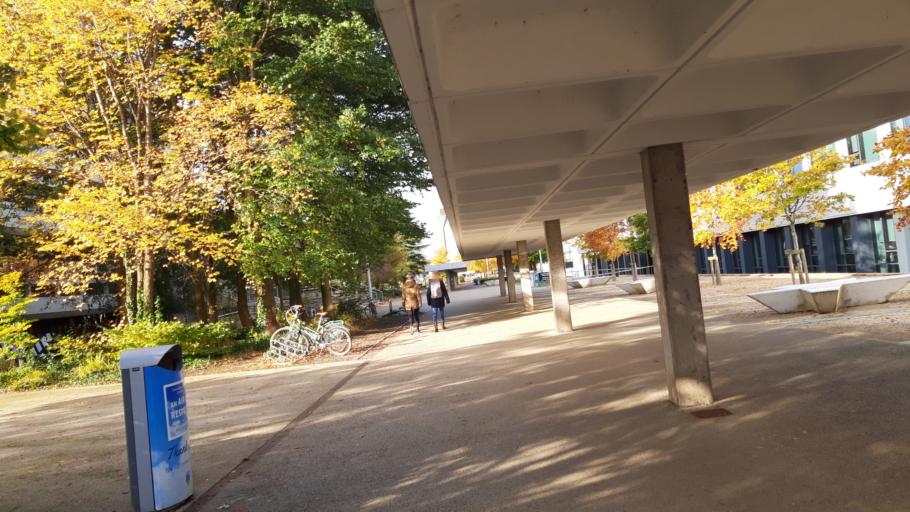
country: IE
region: Leinster
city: Donnybrook
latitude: 53.3074
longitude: -6.2238
